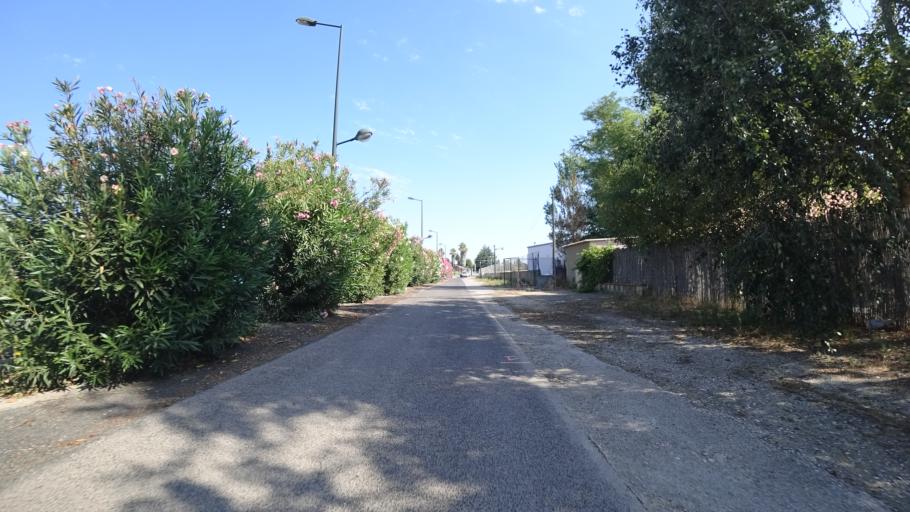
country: FR
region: Languedoc-Roussillon
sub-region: Departement des Pyrenees-Orientales
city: Bompas
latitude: 42.7290
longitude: 2.9250
